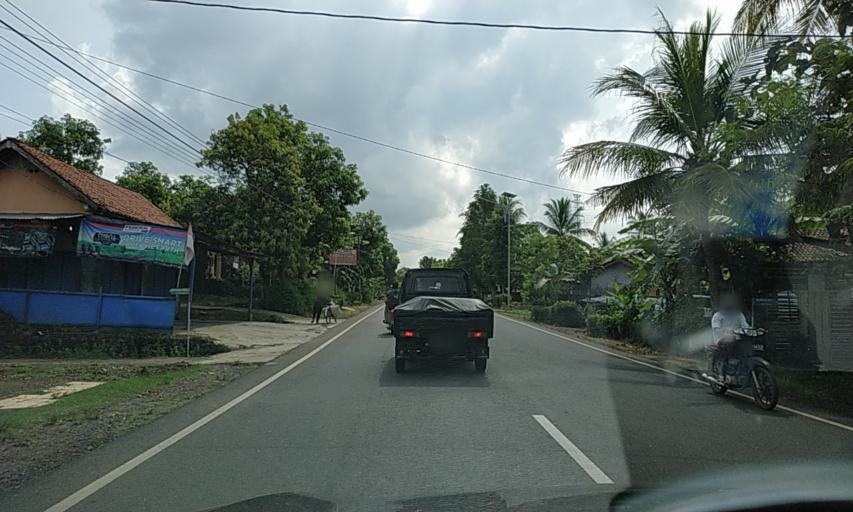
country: ID
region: Central Java
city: Cihandiwung Lor
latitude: -7.3386
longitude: 108.7006
